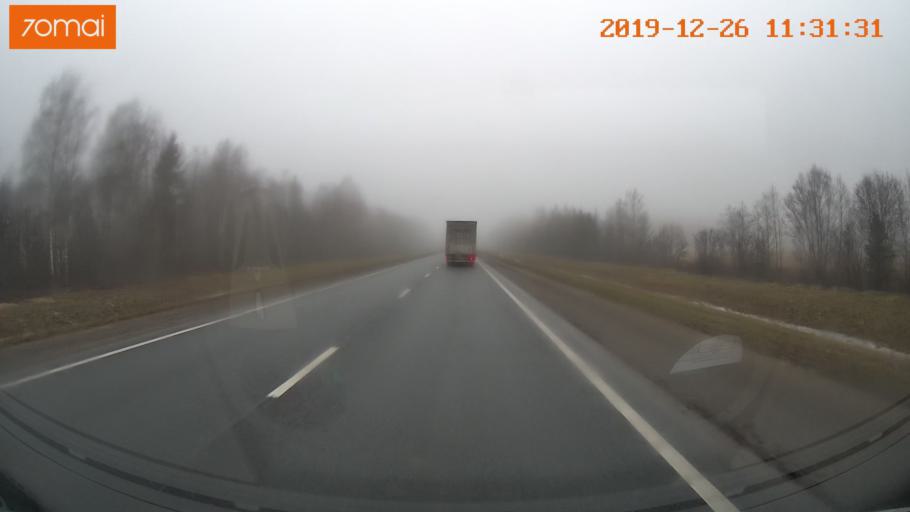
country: RU
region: Vologda
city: Chebsara
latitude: 59.1696
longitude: 38.7513
